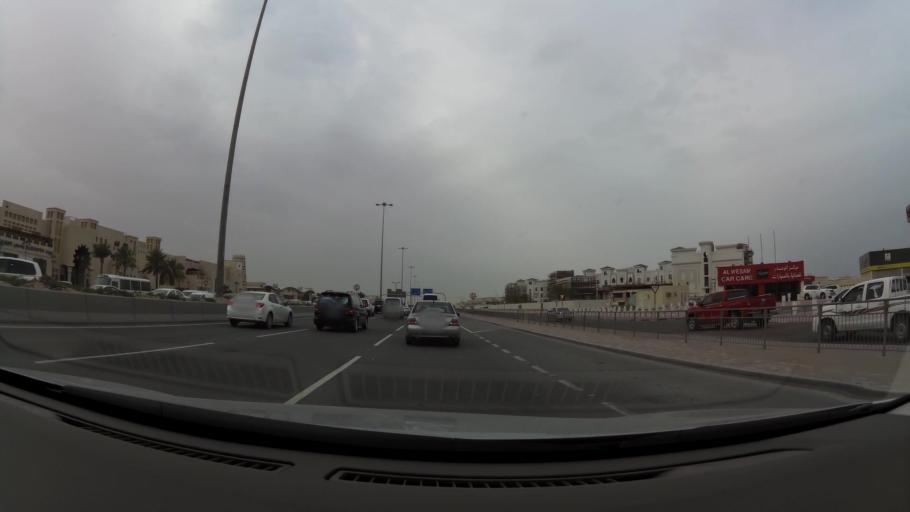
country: QA
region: Baladiyat ar Rayyan
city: Ar Rayyan
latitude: 25.3358
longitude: 51.4626
